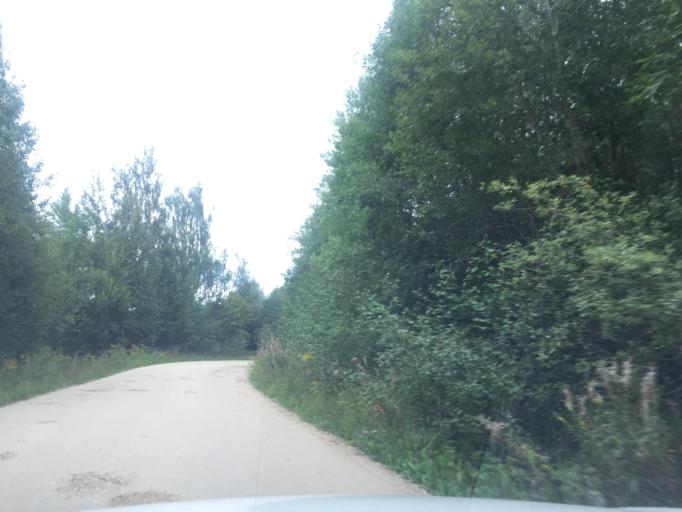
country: RU
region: Leningrad
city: Siverskiy
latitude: 59.2985
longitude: 30.0238
